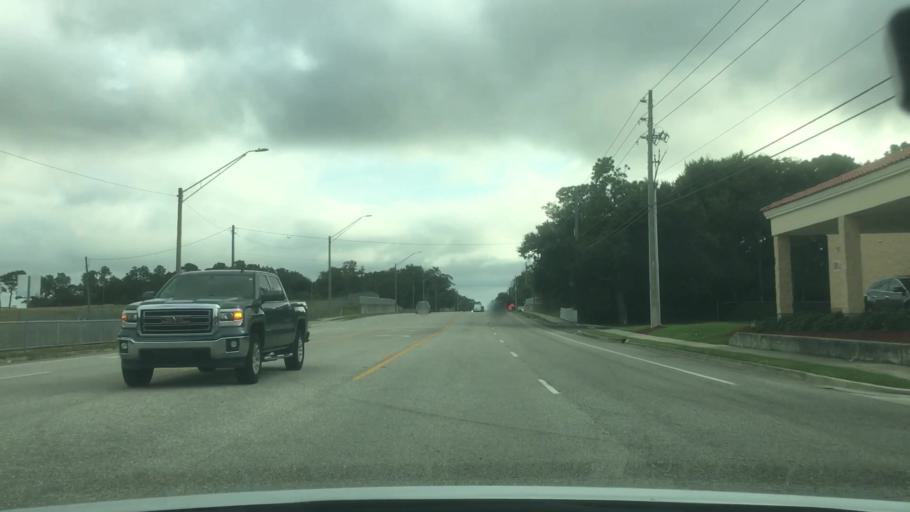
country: US
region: Florida
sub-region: Duval County
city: Atlantic Beach
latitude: 30.3465
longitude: -81.5236
